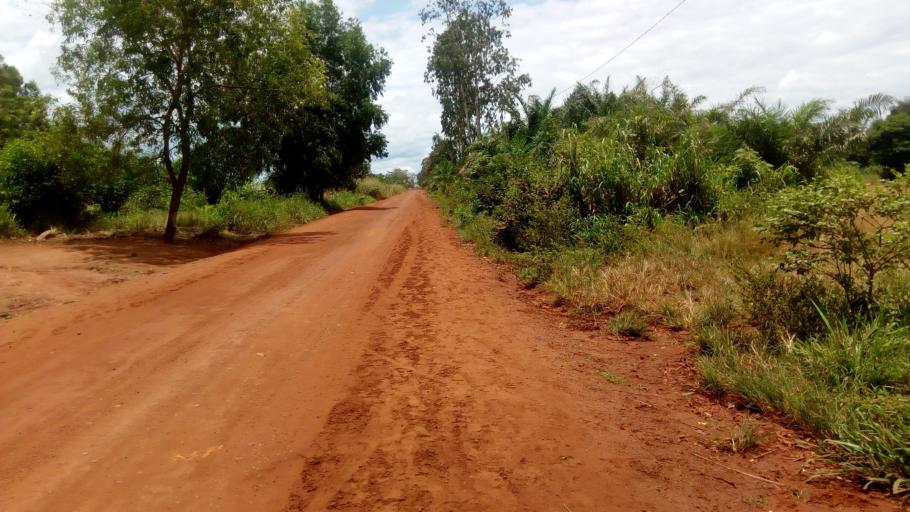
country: TG
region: Maritime
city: Tsevie
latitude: 6.3335
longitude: 1.0854
